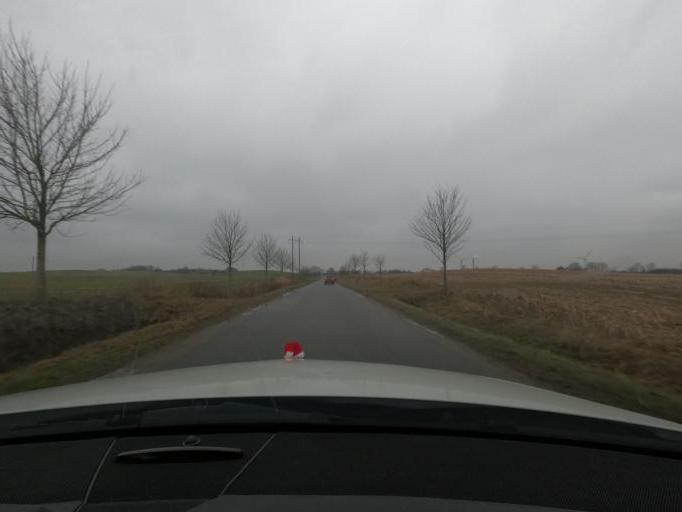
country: DK
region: South Denmark
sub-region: Haderslev Kommune
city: Haderslev
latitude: 55.1949
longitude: 9.4773
